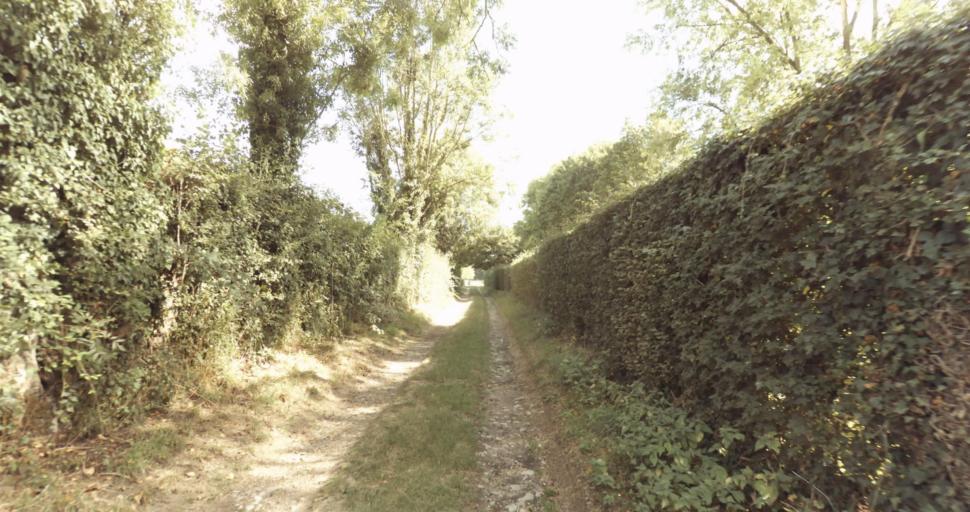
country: FR
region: Lower Normandy
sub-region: Departement de l'Orne
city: Vimoutiers
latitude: 48.9231
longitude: 0.2386
